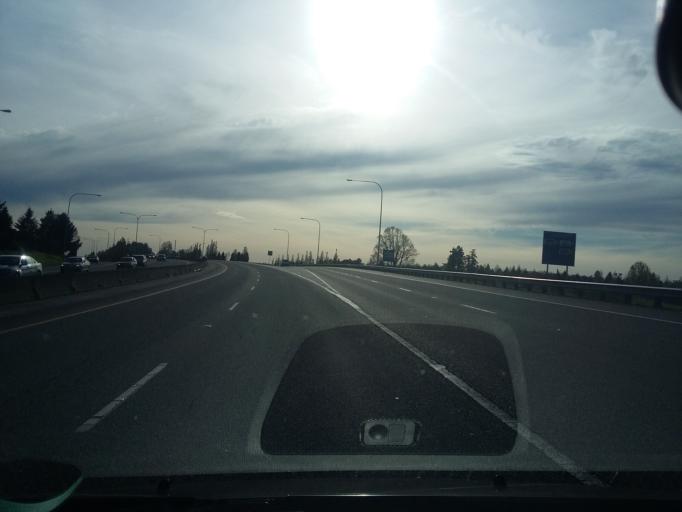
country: US
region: Washington
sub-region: Clark County
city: Walnut Grove
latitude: 45.6560
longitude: -122.5827
